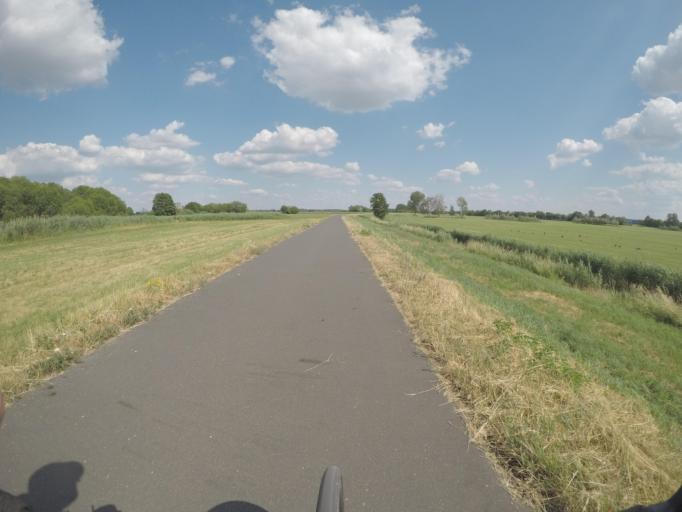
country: DE
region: Brandenburg
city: Ketzin
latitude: 52.4595
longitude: 12.8622
